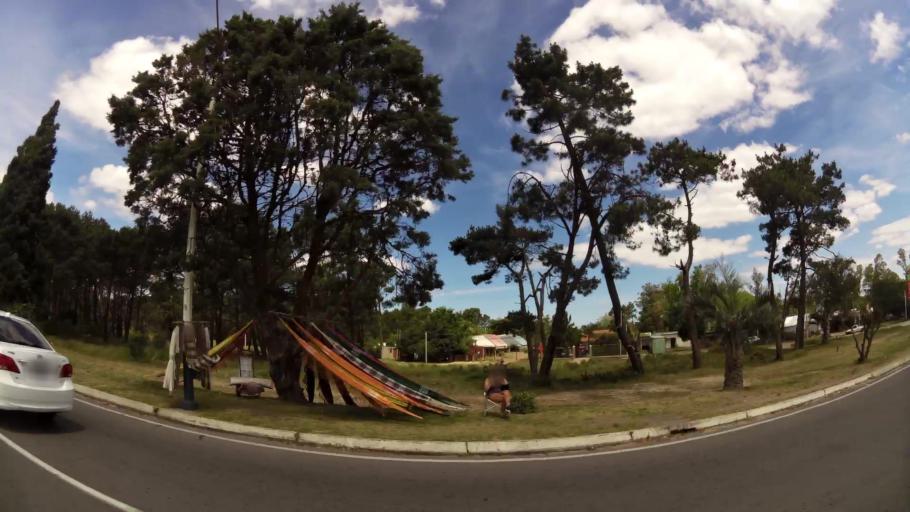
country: UY
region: Canelones
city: Empalme Olmos
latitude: -34.7841
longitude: -55.8871
